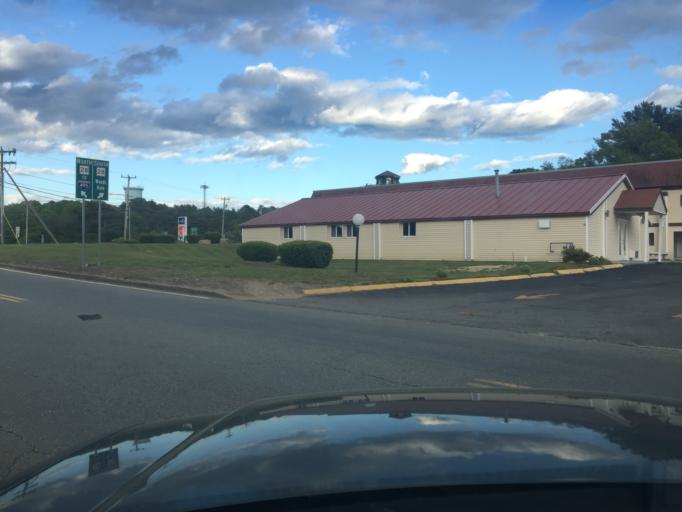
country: US
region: Massachusetts
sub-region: Barnstable County
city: Bourne
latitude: 41.7428
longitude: -70.5881
